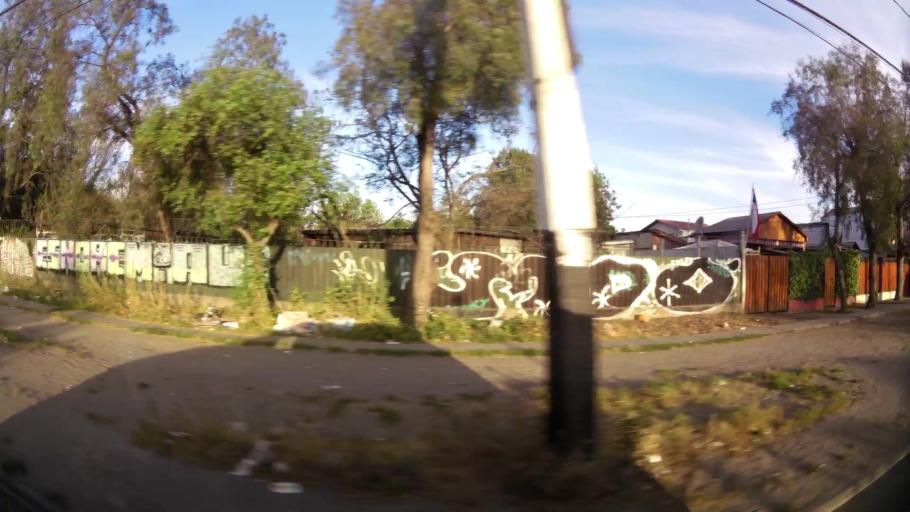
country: CL
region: Santiago Metropolitan
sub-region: Provincia de Santiago
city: Lo Prado
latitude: -33.4374
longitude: -70.7217
